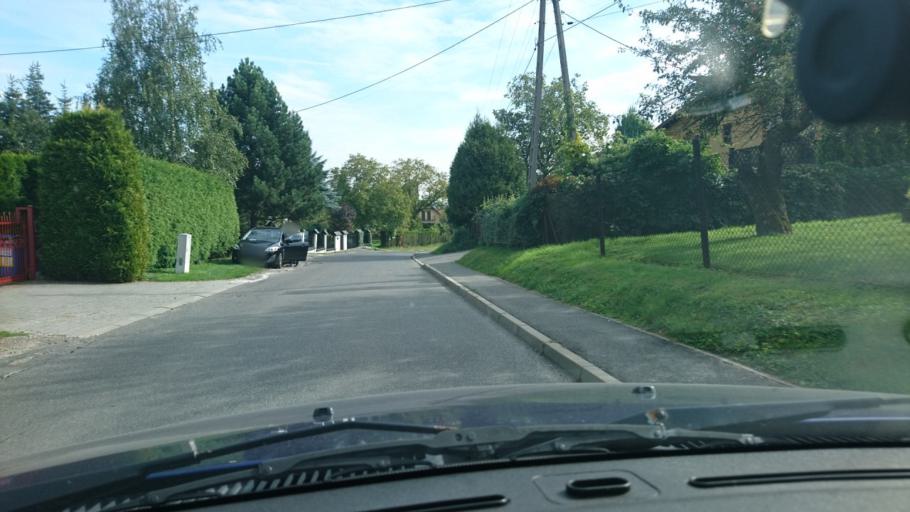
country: PL
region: Silesian Voivodeship
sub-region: Bielsko-Biala
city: Bielsko-Biala
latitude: 49.8232
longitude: 19.0066
